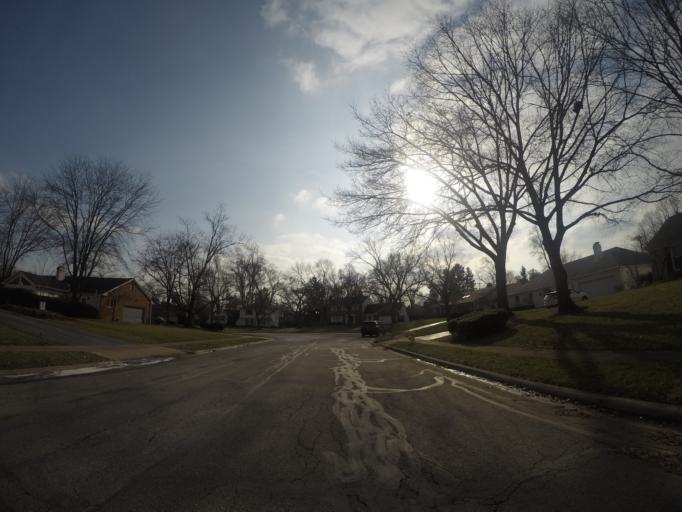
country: US
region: Ohio
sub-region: Franklin County
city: Upper Arlington
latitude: 40.0420
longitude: -83.0568
